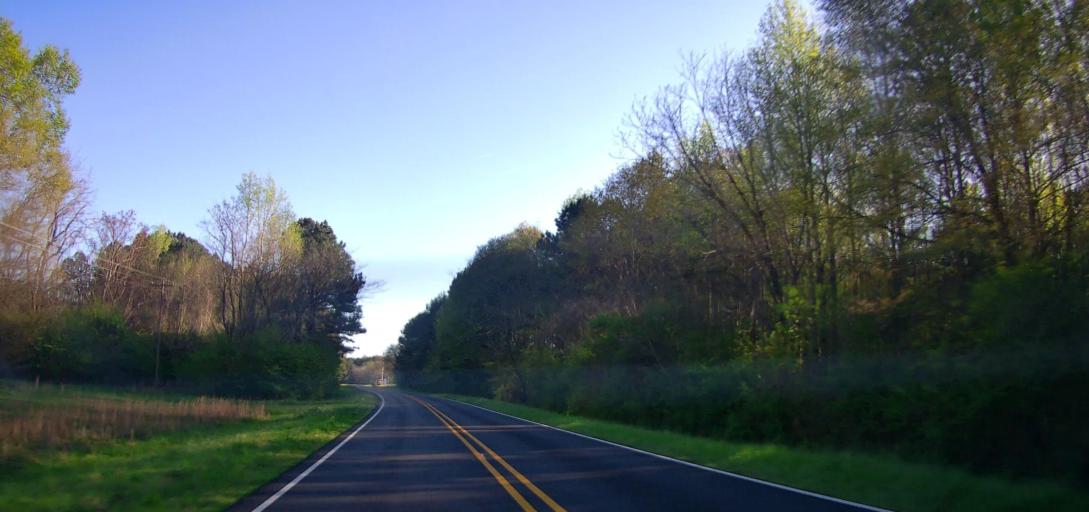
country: US
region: Georgia
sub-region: Butts County
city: Jackson
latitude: 33.3409
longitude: -83.9102
